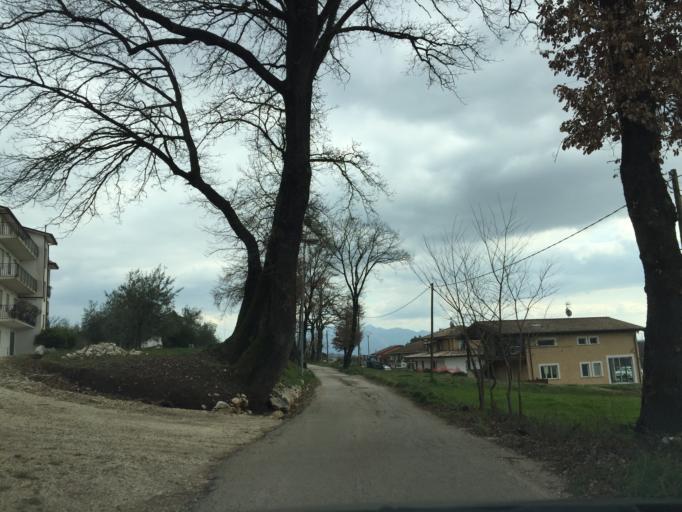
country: IT
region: Latium
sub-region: Provincia di Frosinone
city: Cassino
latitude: 41.4835
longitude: 13.8008
